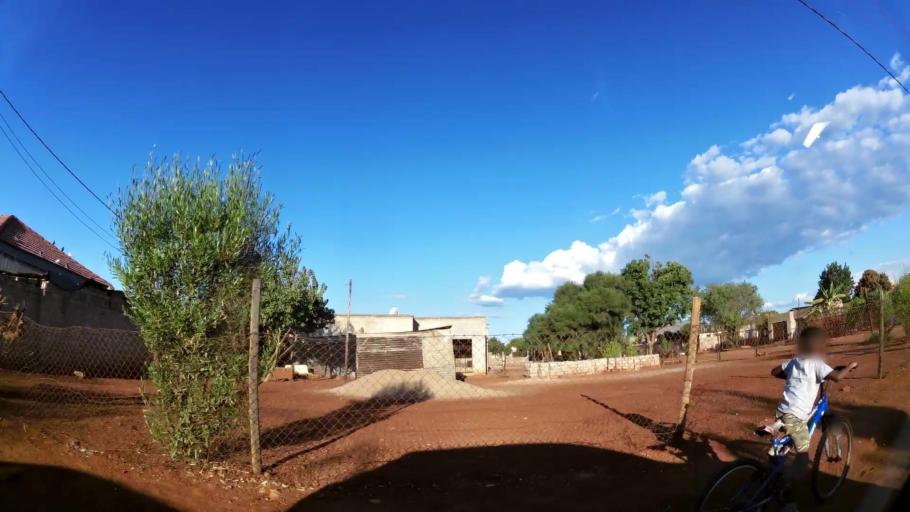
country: ZA
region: Limpopo
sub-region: Waterberg District Municipality
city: Mokopane
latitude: -24.1501
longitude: 28.9948
